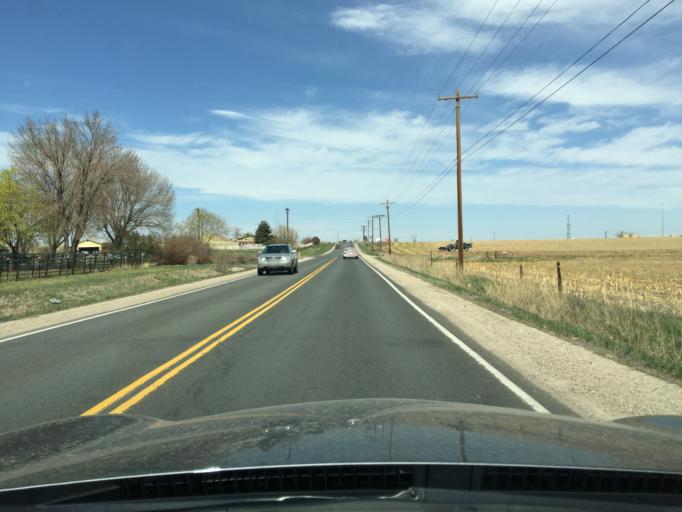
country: US
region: Colorado
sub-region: Boulder County
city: Erie
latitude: 39.9784
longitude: -104.9972
